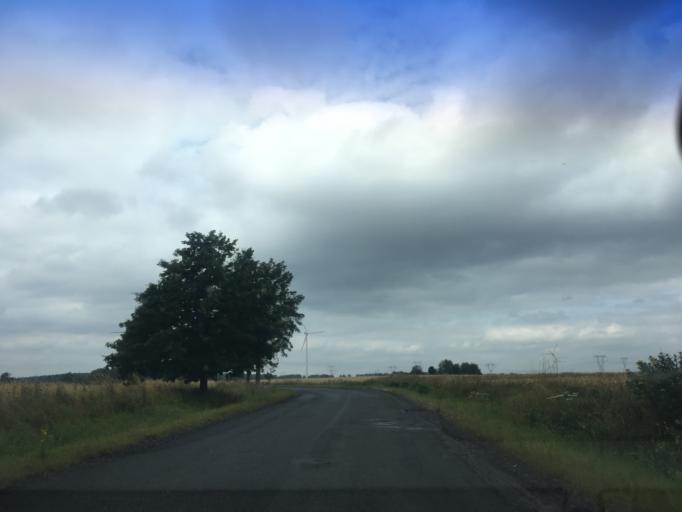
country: PL
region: Lower Silesian Voivodeship
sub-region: Powiat zgorzelecki
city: Sulikow
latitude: 51.0797
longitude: 15.0537
